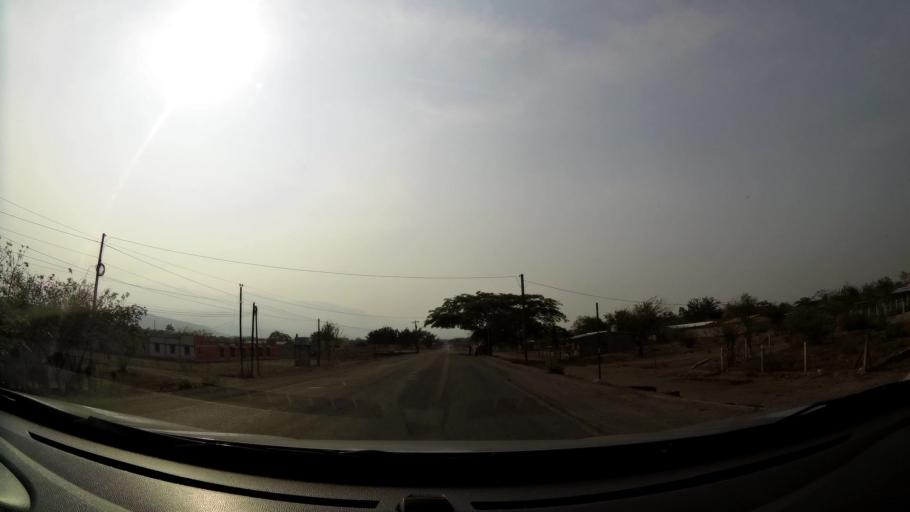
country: HN
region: Comayagua
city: Comayagua
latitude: 14.4619
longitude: -87.6672
